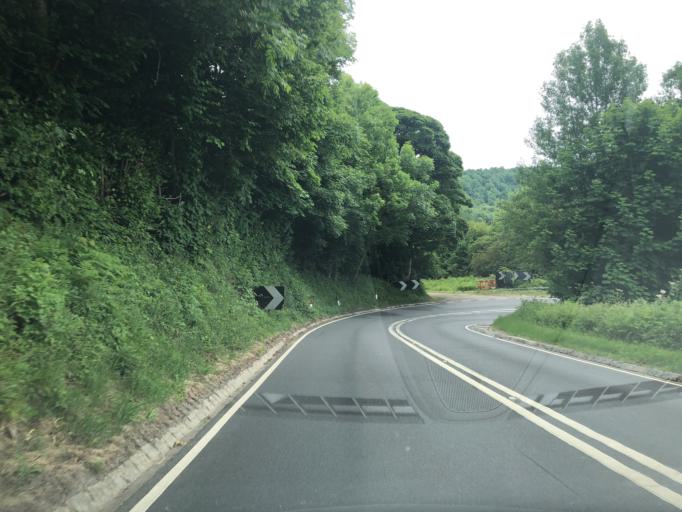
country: GB
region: England
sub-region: North Yorkshire
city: Angram Grange
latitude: 54.2368
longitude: -1.2098
